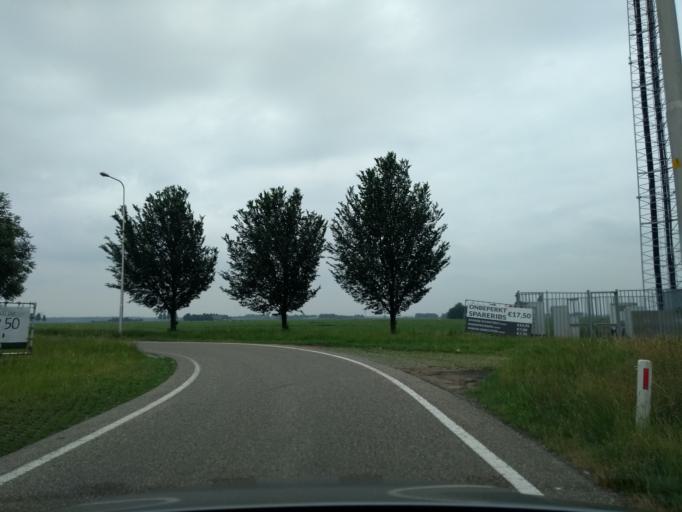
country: NL
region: Overijssel
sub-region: Gemeente Kampen
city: Kampen
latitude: 52.5057
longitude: 5.9697
